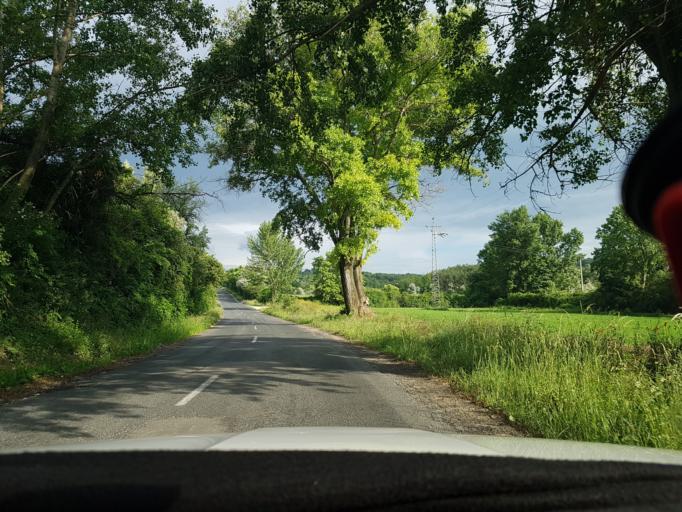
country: HU
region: Komarom-Esztergom
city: Labatlan
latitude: 47.7308
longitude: 18.5295
